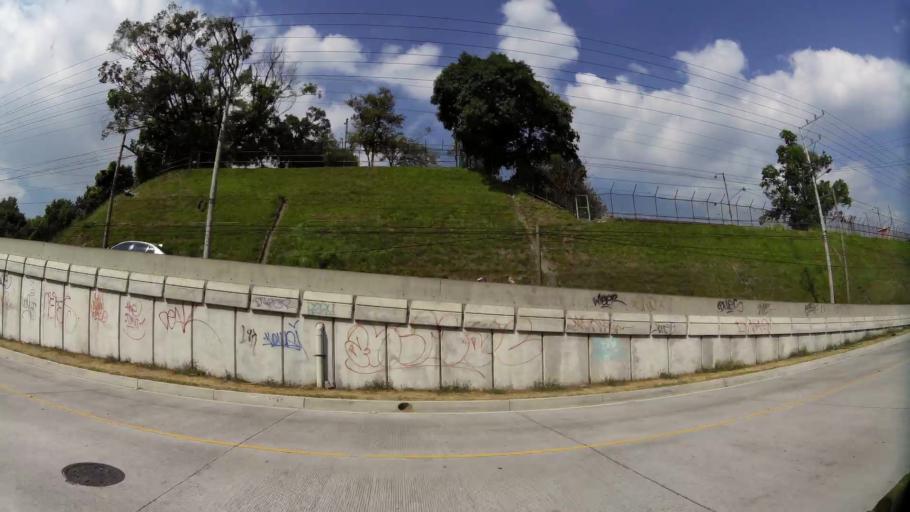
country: SV
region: San Salvador
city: San Salvador
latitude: 13.6995
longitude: -89.1728
